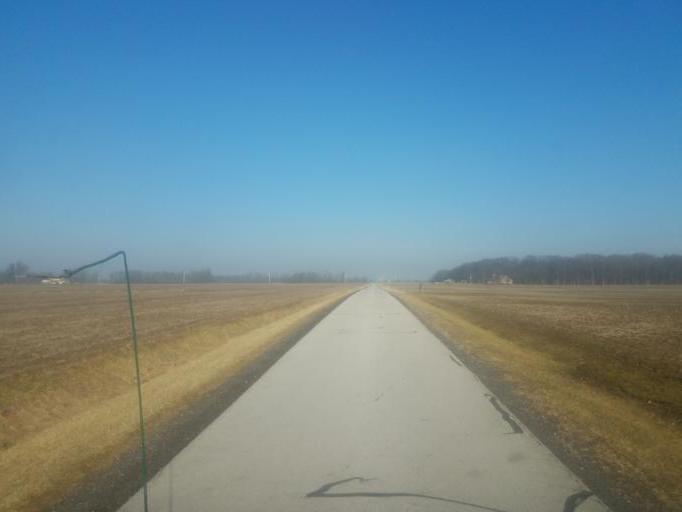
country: US
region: Ohio
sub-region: Seneca County
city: Tiffin
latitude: 41.0473
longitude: -83.1129
